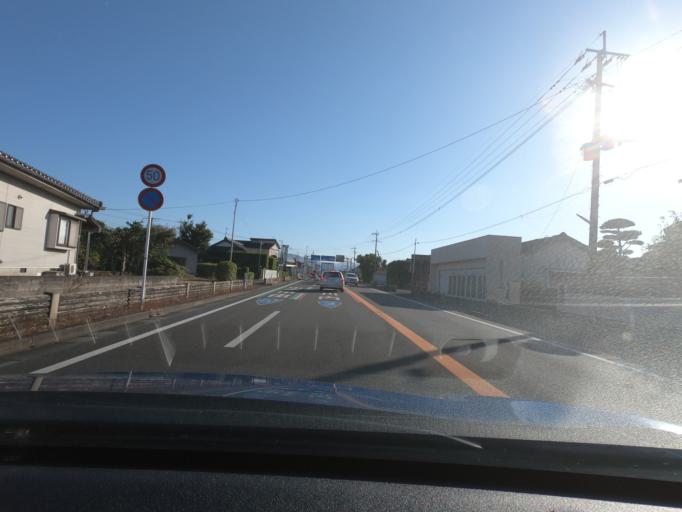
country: JP
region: Kagoshima
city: Izumi
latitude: 32.1192
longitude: 130.3400
